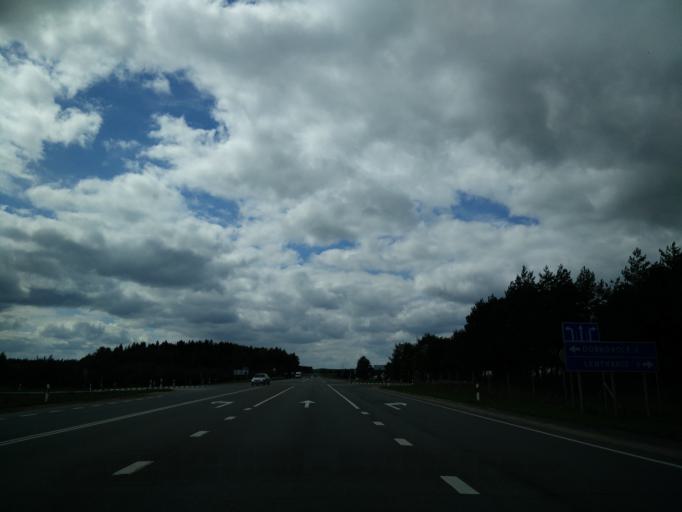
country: LT
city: Lentvaris
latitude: 54.6197
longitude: 25.0676
